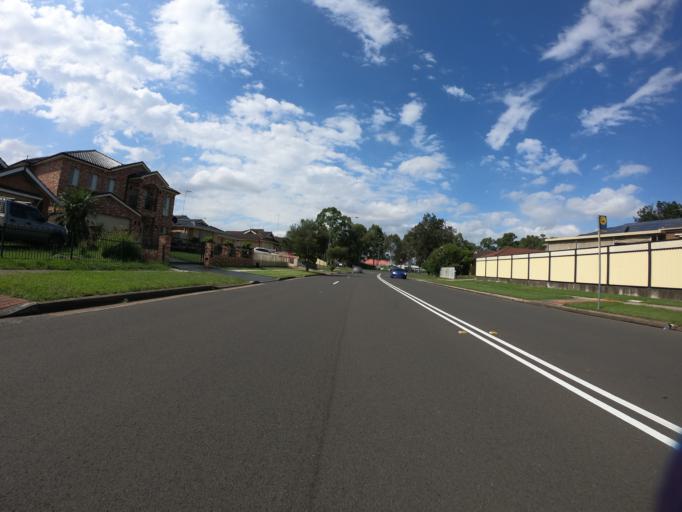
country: AU
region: New South Wales
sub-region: Blacktown
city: Hassall Grove
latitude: -33.7367
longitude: 150.8367
